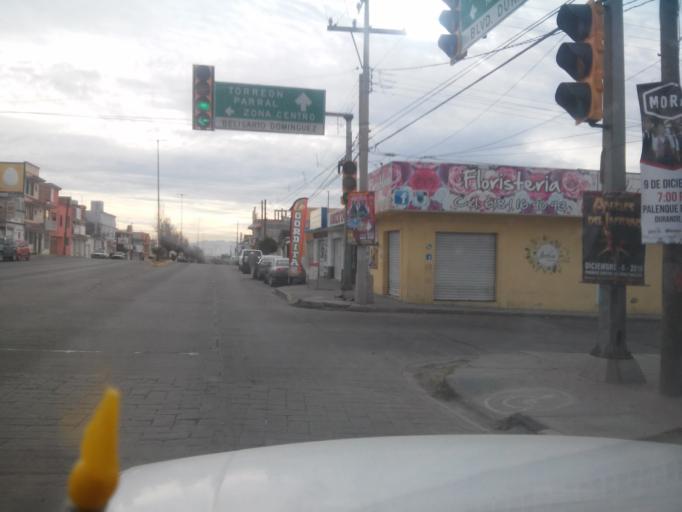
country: MX
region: Durango
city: Victoria de Durango
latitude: 24.0137
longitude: -104.6753
